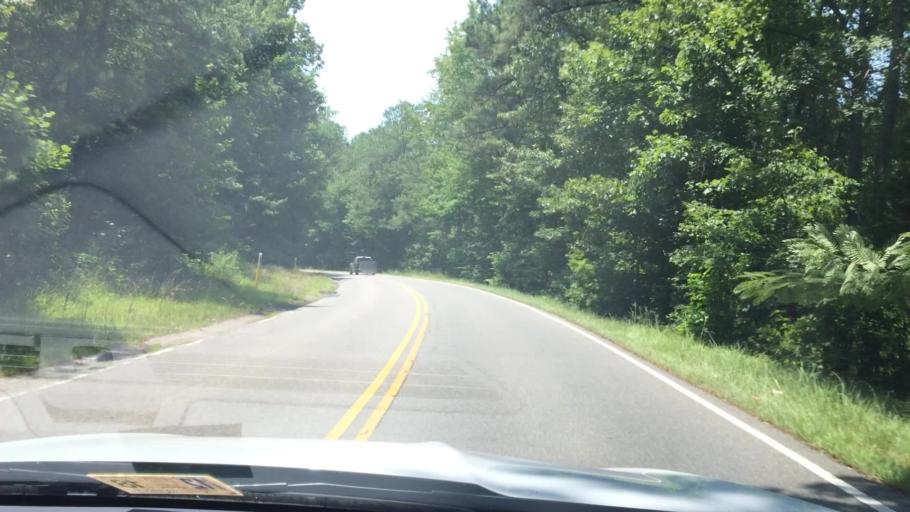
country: US
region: Virginia
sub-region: City of Williamsburg
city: Williamsburg
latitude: 37.2817
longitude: -76.6250
